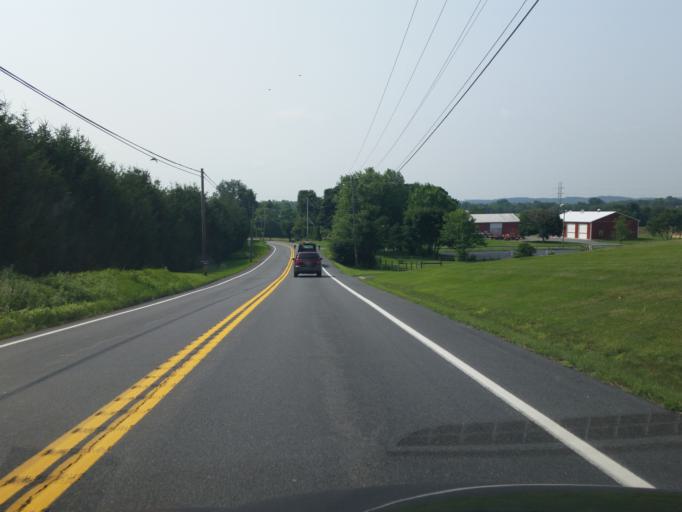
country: US
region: Pennsylvania
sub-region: Dauphin County
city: Palmdale
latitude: 40.3545
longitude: -76.6395
